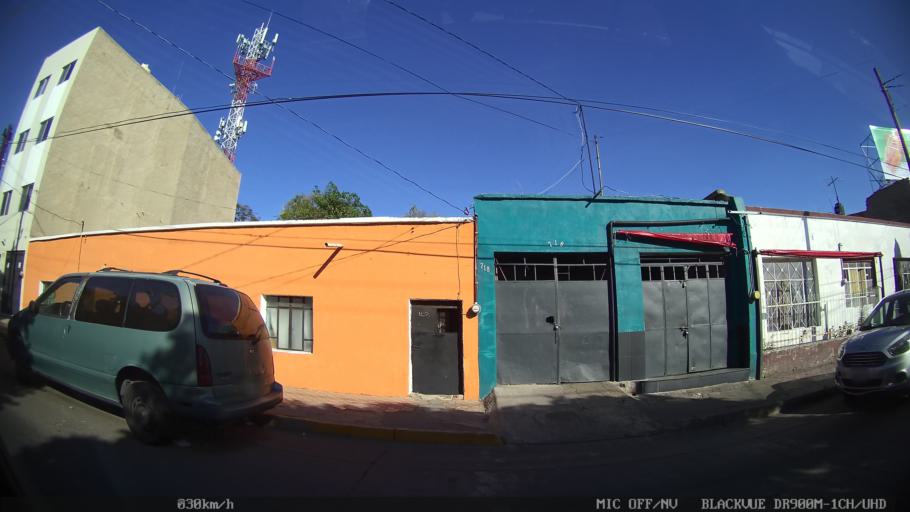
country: MX
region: Jalisco
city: Tlaquepaque
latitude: 20.6832
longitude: -103.3268
